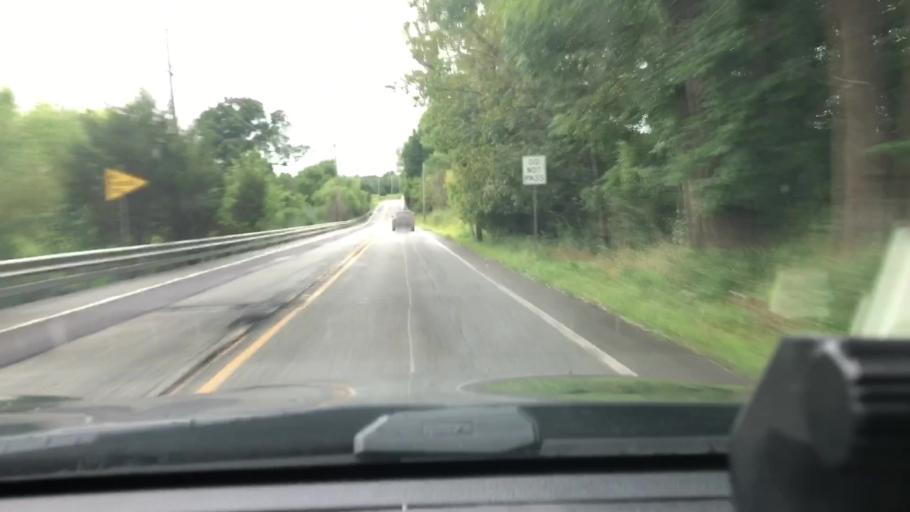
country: US
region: Pennsylvania
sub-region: Montgomery County
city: Gilbertsville
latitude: 40.3220
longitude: -75.5636
